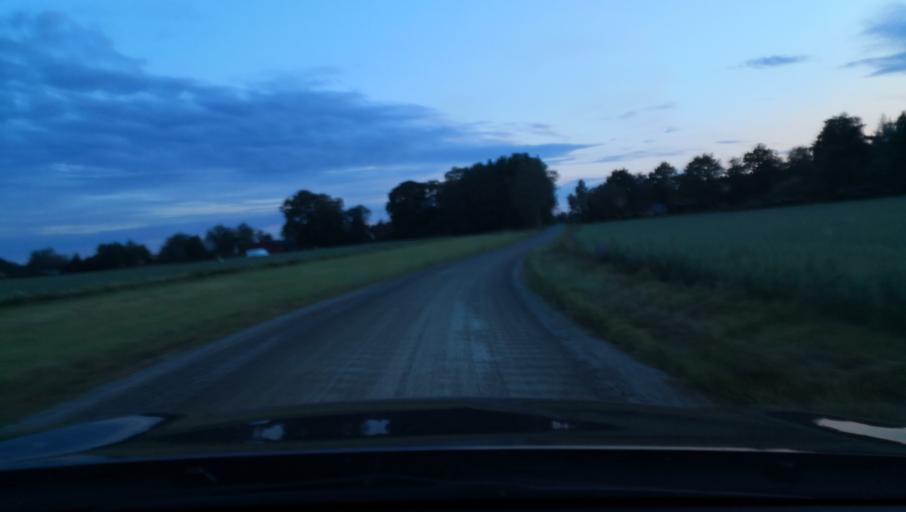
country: SE
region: Uppsala
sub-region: Osthammars Kommun
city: Bjorklinge
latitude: 60.0019
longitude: 17.3674
